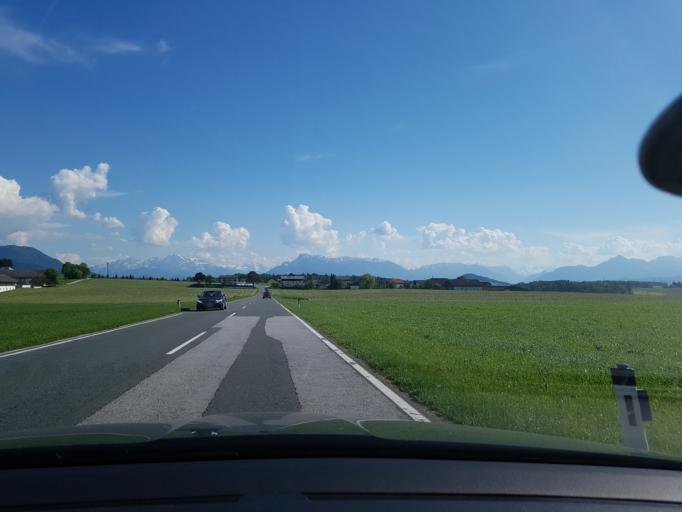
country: AT
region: Salzburg
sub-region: Politischer Bezirk Salzburg-Umgebung
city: Obertrum am See
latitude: 47.9039
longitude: 13.0797
